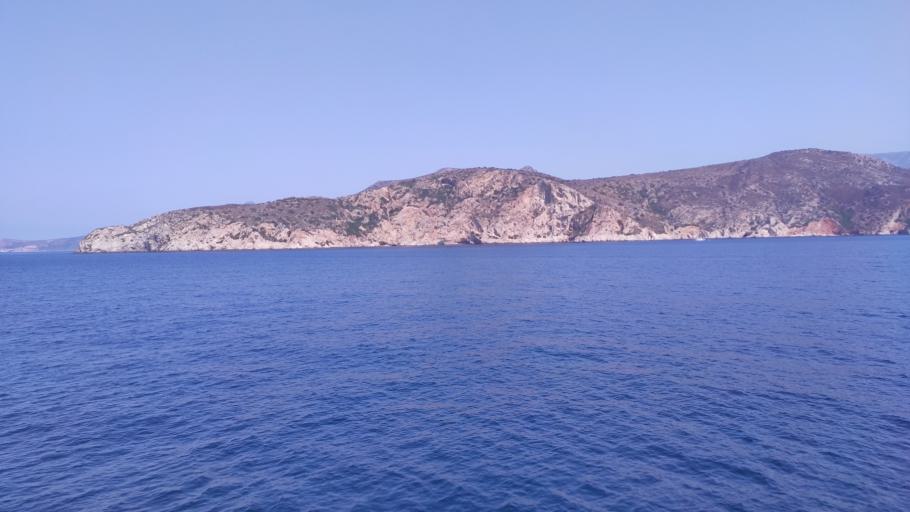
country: TR
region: Mugla
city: Datca
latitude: 36.6431
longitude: 27.4899
